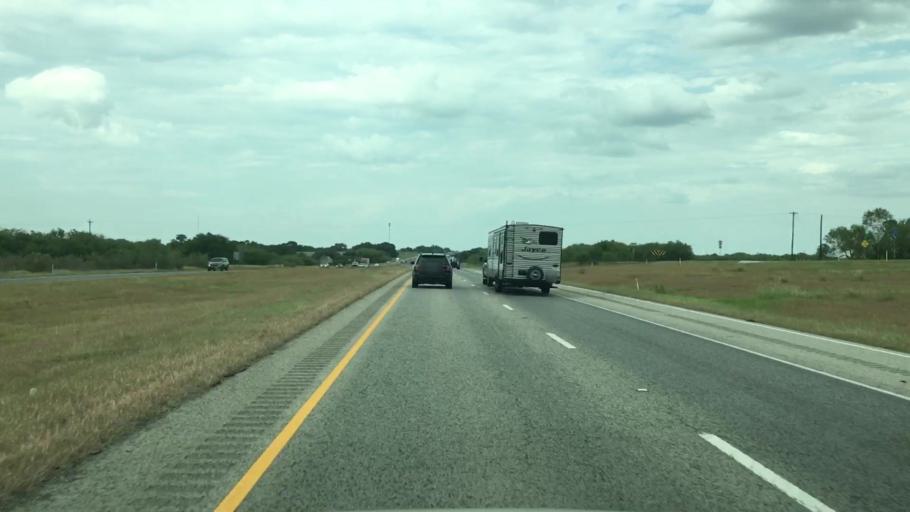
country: US
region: Texas
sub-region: Atascosa County
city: Pleasanton
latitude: 29.1084
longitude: -98.4322
